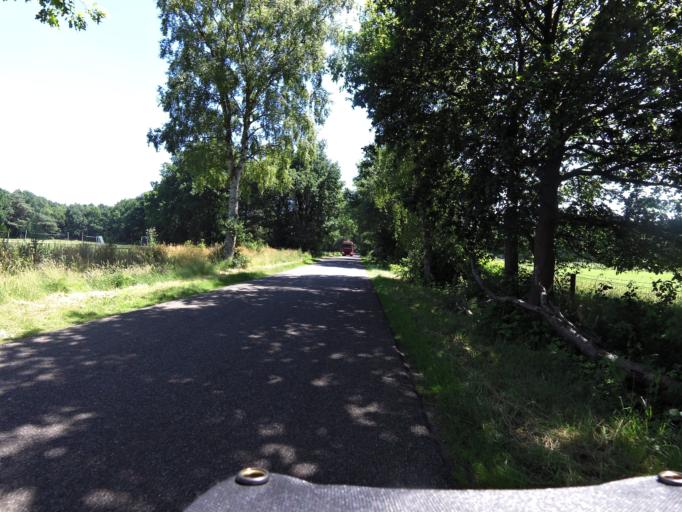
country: NL
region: Overijssel
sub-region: Gemeente Twenterand
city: Den Ham
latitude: 52.4870
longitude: 6.4120
